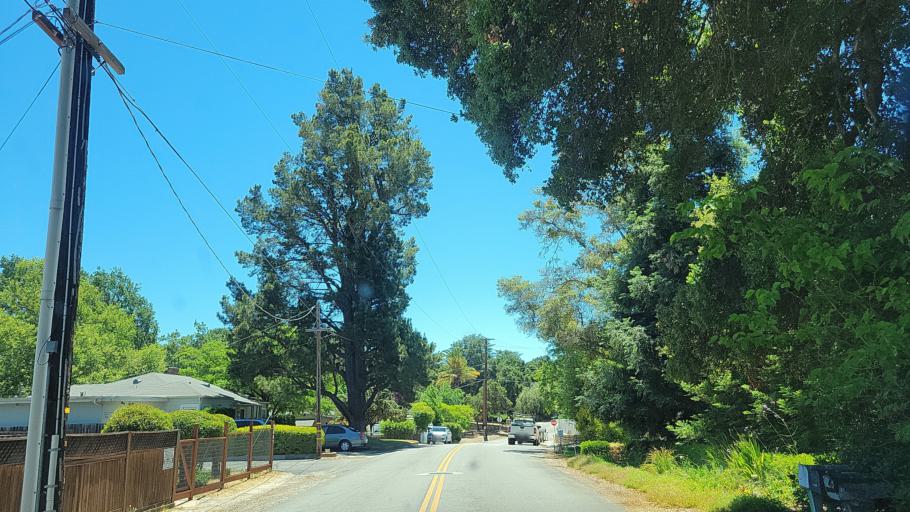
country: US
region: California
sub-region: San Luis Obispo County
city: Atascadero
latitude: 35.4937
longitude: -120.6703
